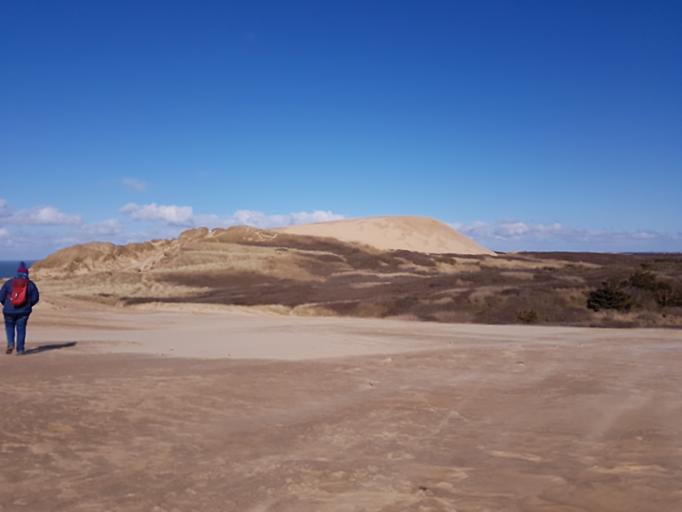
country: DK
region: North Denmark
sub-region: Hjorring Kommune
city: Vra
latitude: 57.4437
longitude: 9.7719
